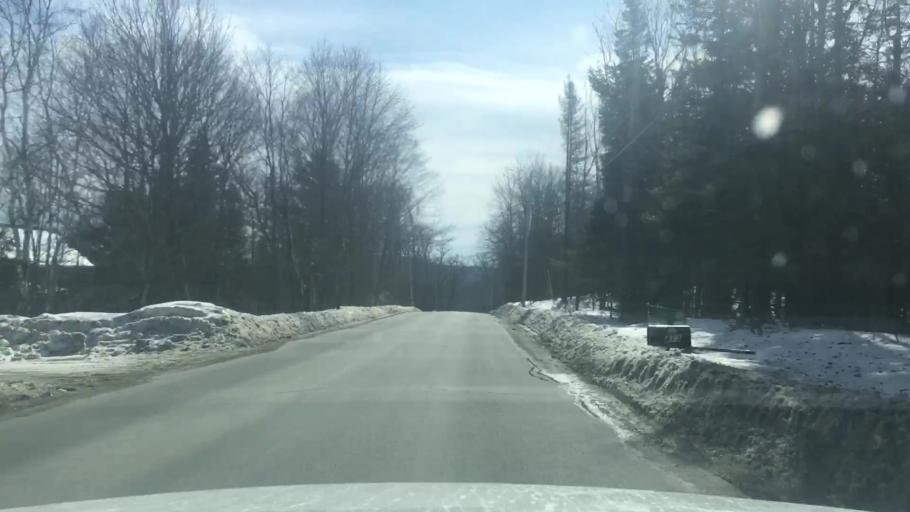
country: US
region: Maine
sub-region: Penobscot County
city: Holden
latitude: 44.7632
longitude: -68.6422
